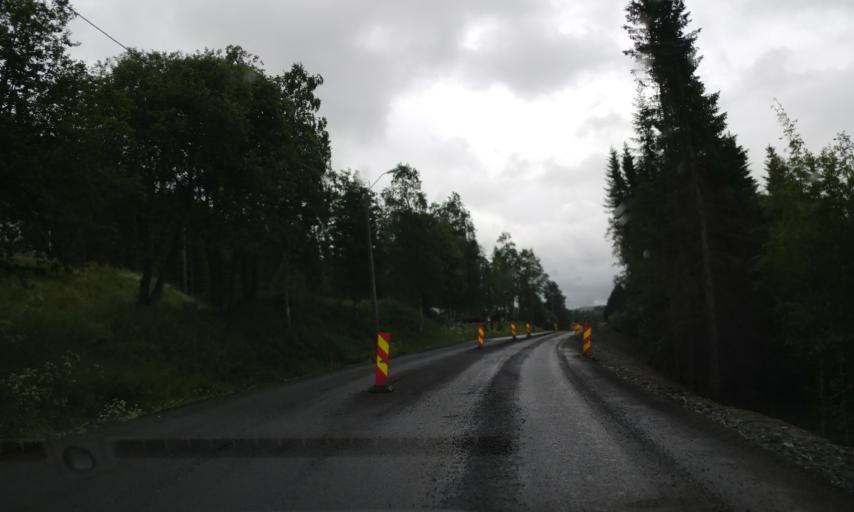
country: NO
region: Sor-Trondelag
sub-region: Selbu
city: Mebonden
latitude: 63.2839
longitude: 11.0801
